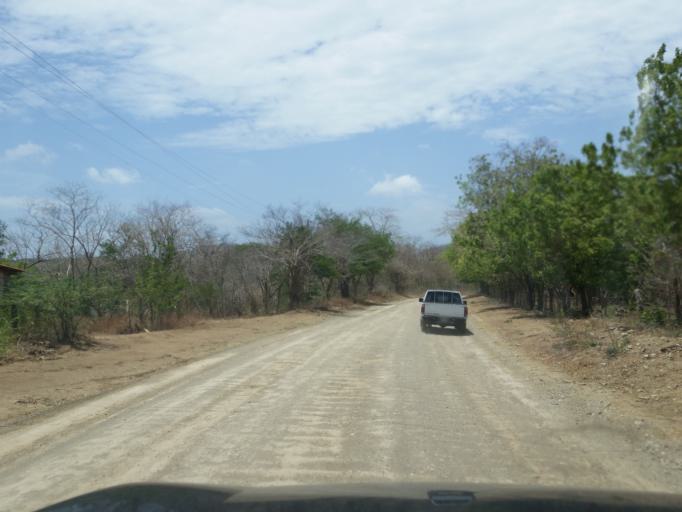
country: NI
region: Rivas
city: Tola
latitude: 11.4669
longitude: -86.0912
